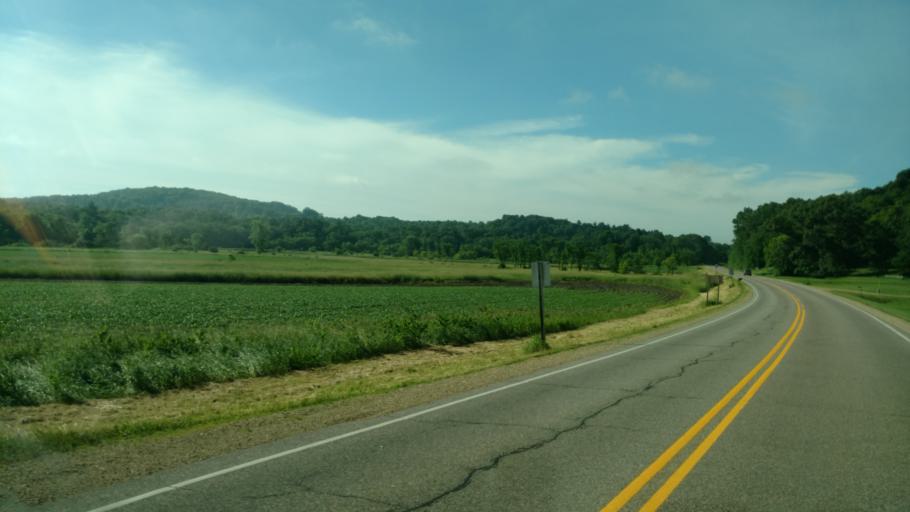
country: US
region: Wisconsin
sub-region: Sauk County
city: Reedsburg
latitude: 43.5774
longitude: -90.1343
